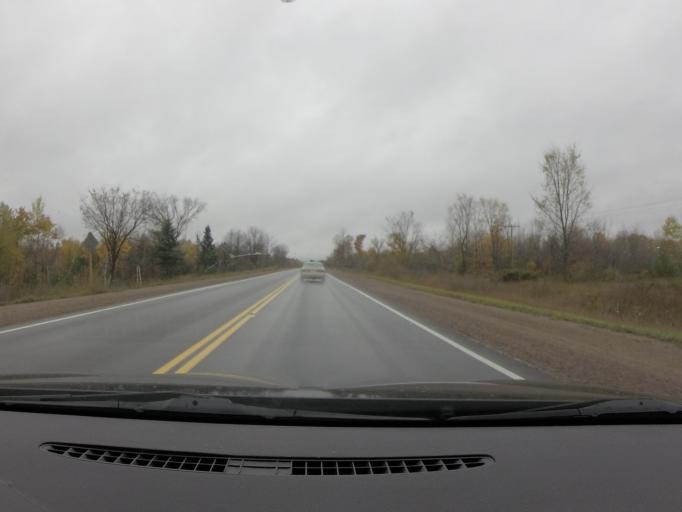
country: CA
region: Ontario
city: Skatepark
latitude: 44.6957
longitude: -77.0194
